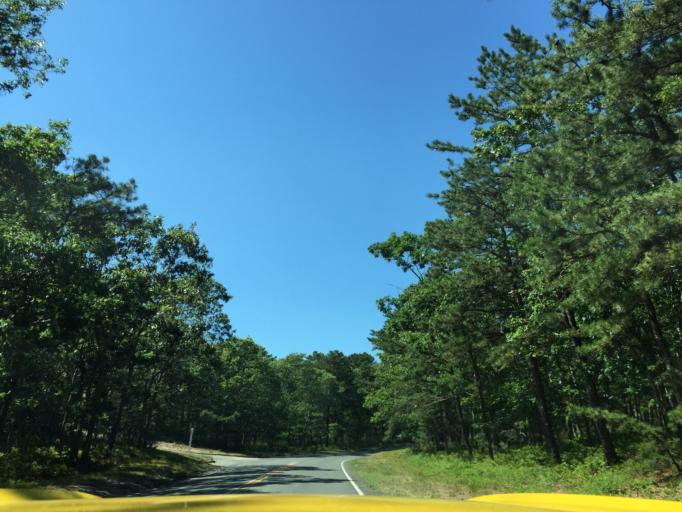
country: US
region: New York
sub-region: Suffolk County
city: Sag Harbor
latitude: 40.9714
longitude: -72.2584
